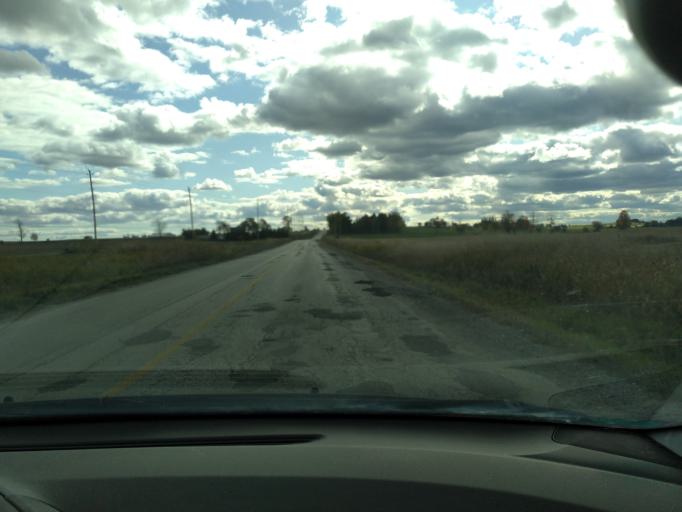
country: CA
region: Ontario
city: Bradford West Gwillimbury
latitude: 44.0921
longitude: -79.5982
